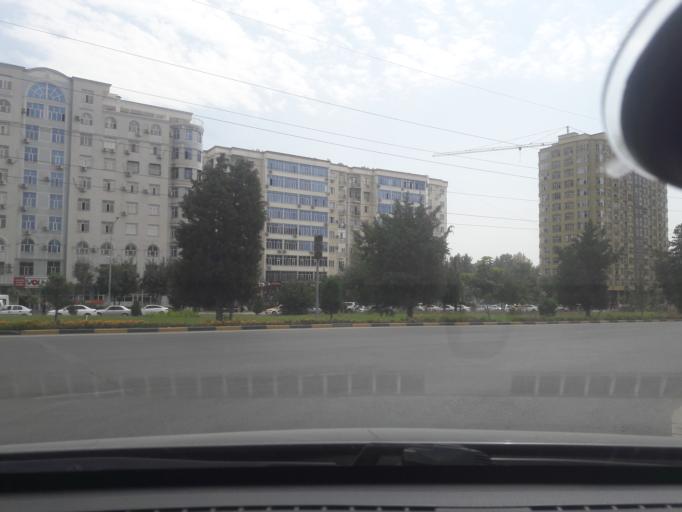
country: TJ
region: Dushanbe
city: Dushanbe
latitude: 38.5911
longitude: 68.7419
